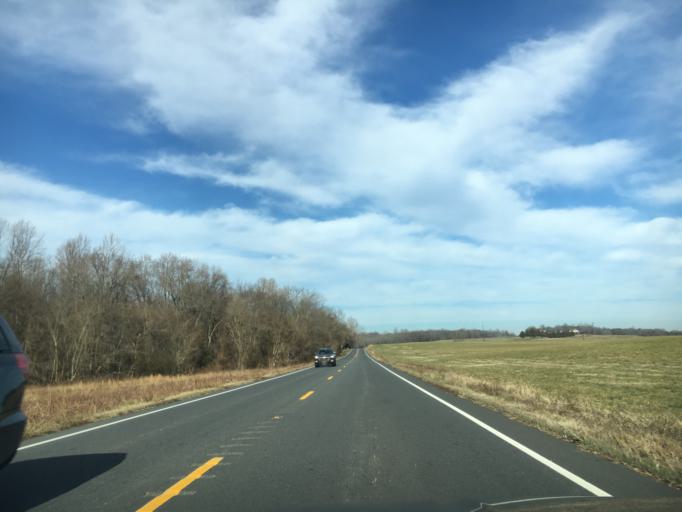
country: US
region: Virginia
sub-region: Culpeper County
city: Culpeper
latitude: 38.3334
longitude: -77.9557
